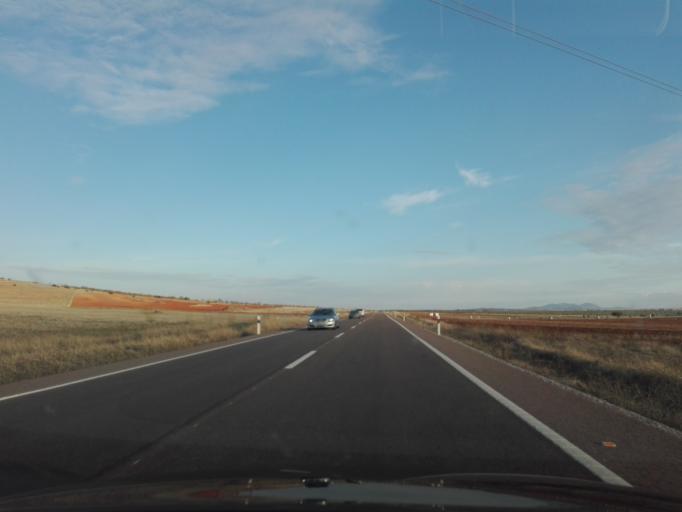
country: ES
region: Extremadura
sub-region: Provincia de Badajoz
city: Usagre
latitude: 38.3576
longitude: -6.2116
